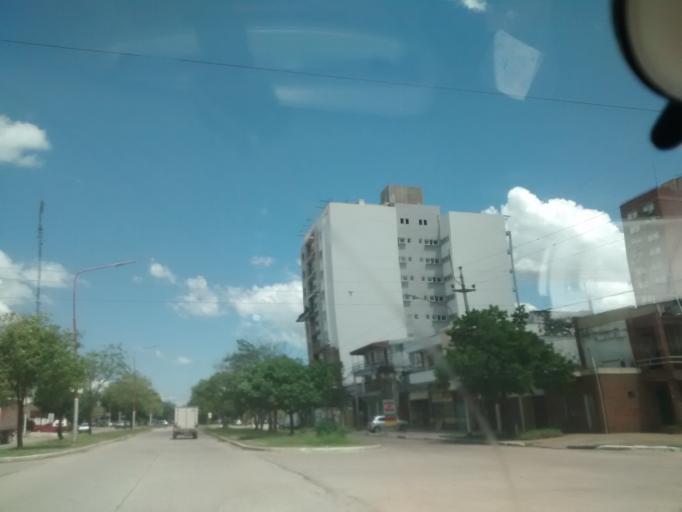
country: AR
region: Chaco
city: Resistencia
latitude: -27.4550
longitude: -58.9963
